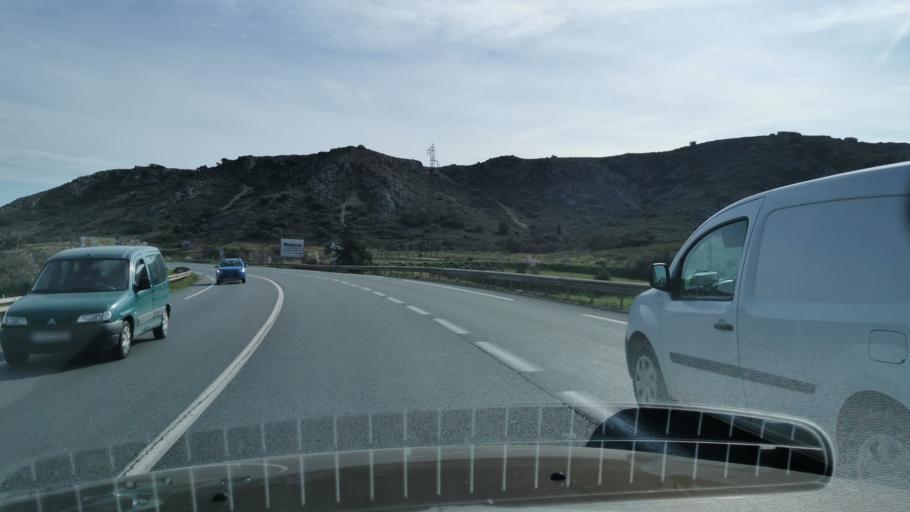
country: FR
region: Languedoc-Roussillon
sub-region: Departement de l'Aude
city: Narbonne
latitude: 43.1796
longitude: 2.9676
